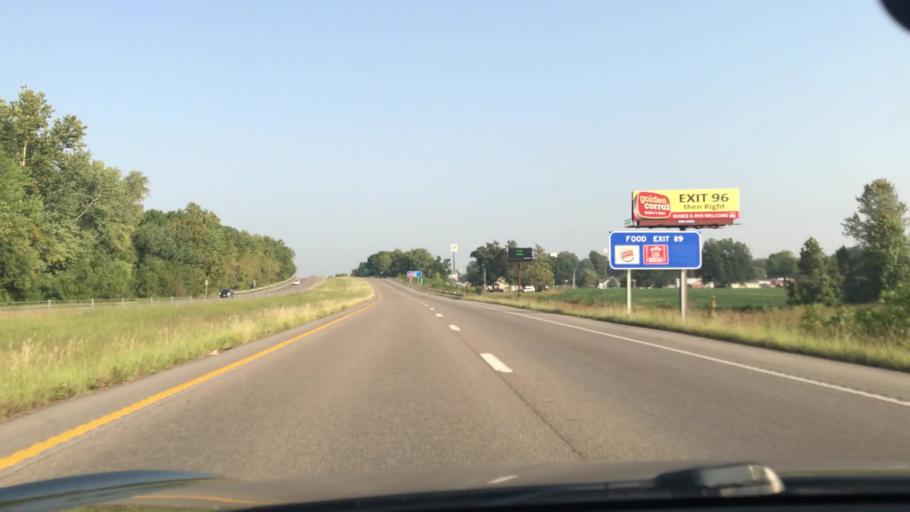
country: US
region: Missouri
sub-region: Scott County
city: Scott City
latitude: 37.2087
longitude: -89.5403
